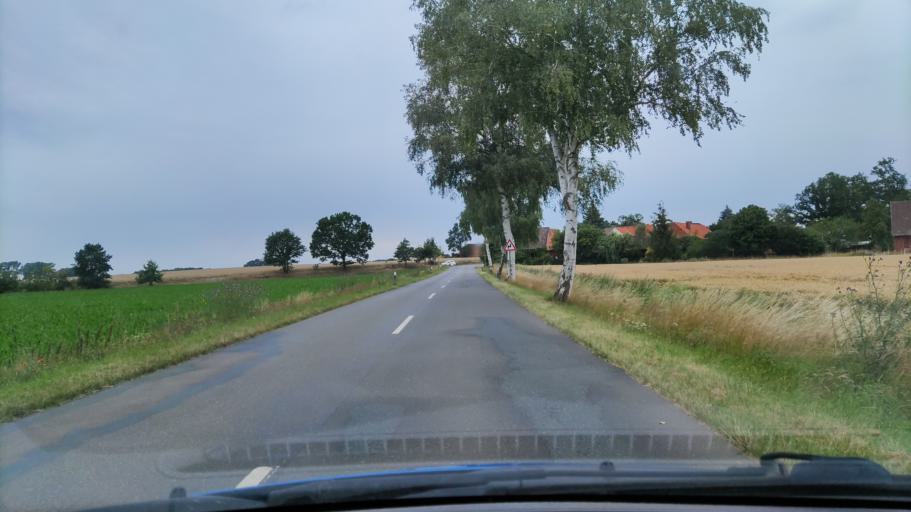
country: DE
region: Lower Saxony
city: Rosche
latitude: 52.9743
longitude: 10.7880
